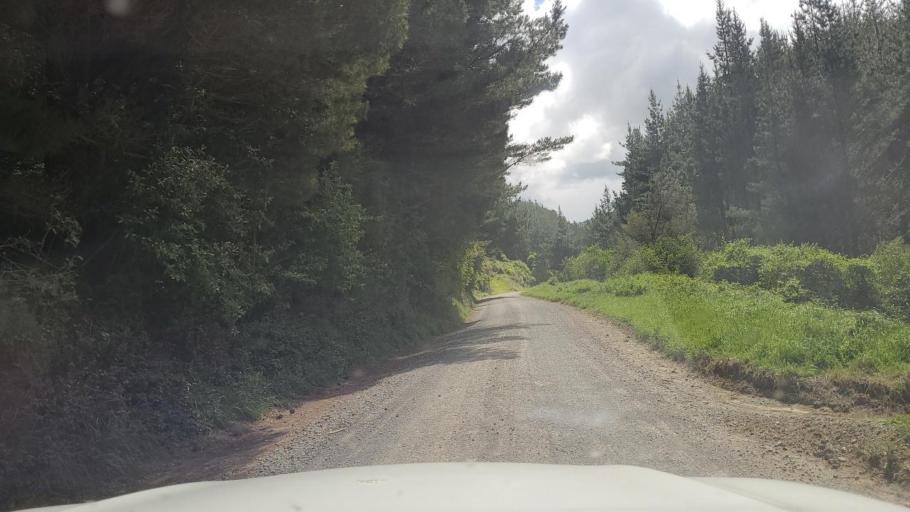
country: NZ
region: Hawke's Bay
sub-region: Napier City
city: Taradale
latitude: -39.2748
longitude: 176.6642
